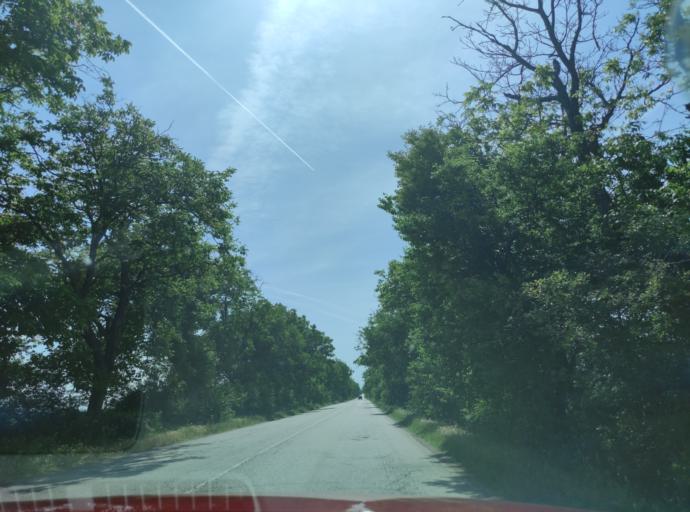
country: BG
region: Pleven
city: Iskur
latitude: 43.4475
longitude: 24.3266
